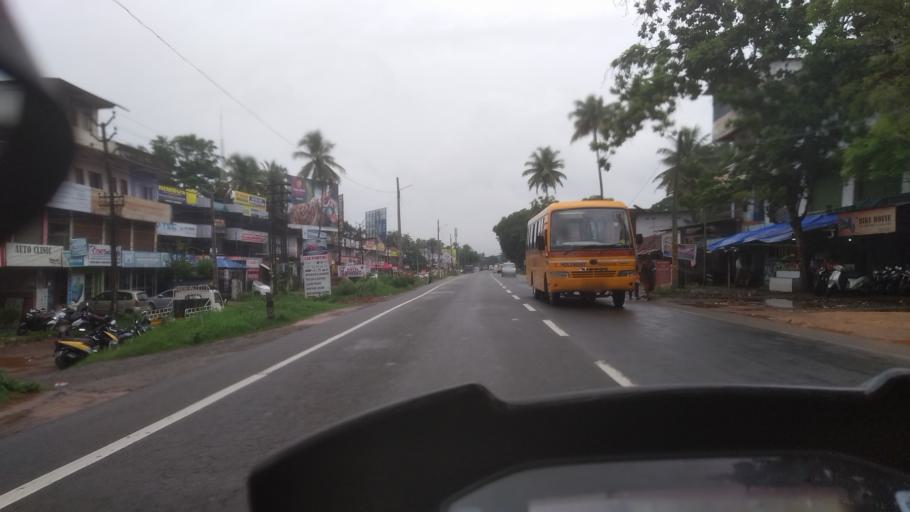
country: IN
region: Kerala
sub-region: Alappuzha
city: Kayankulam
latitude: 9.1768
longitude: 76.4943
